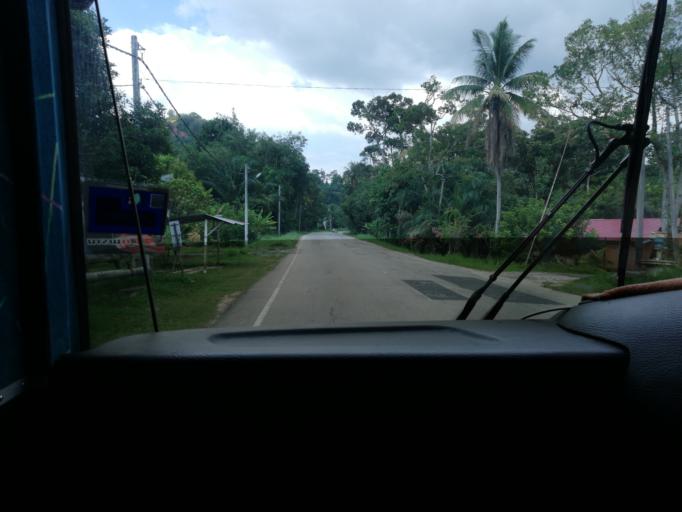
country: MY
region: Perak
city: Parit Buntar
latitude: 5.1308
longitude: 100.5751
